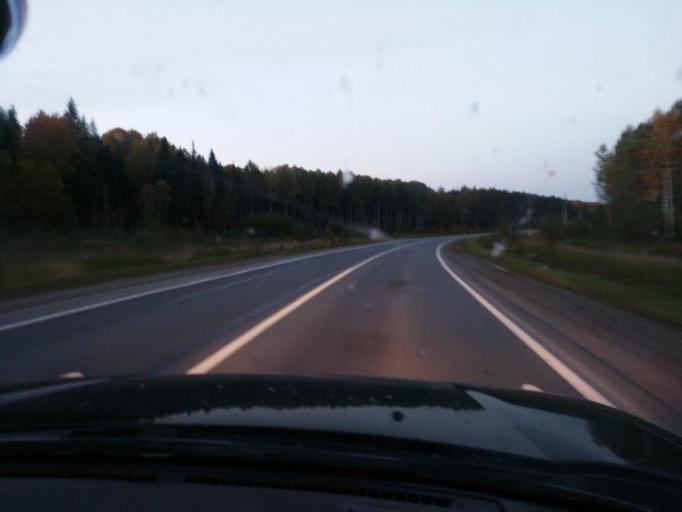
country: RU
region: Perm
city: Verkhnechusovskiye Gorodki
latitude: 58.2371
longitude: 57.2193
